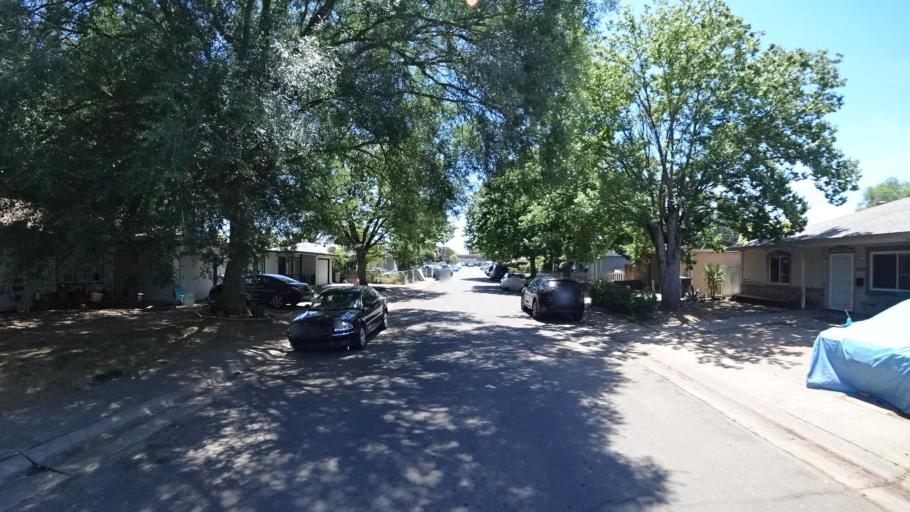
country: US
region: California
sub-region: Sacramento County
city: Florin
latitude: 38.5261
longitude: -121.4209
